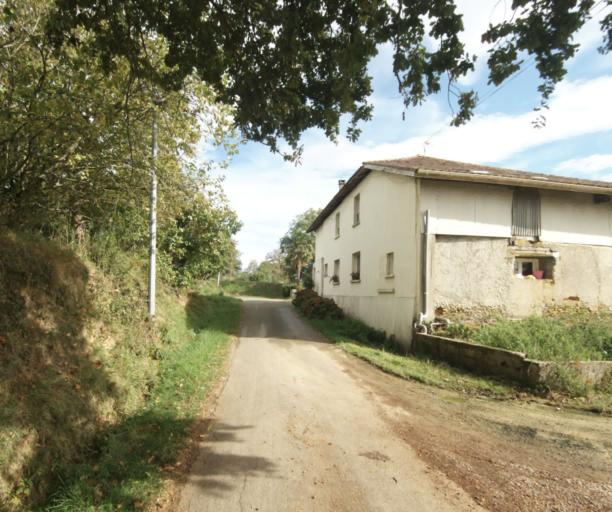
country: FR
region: Midi-Pyrenees
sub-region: Departement du Gers
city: Cazaubon
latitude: 43.8775
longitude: -0.1425
